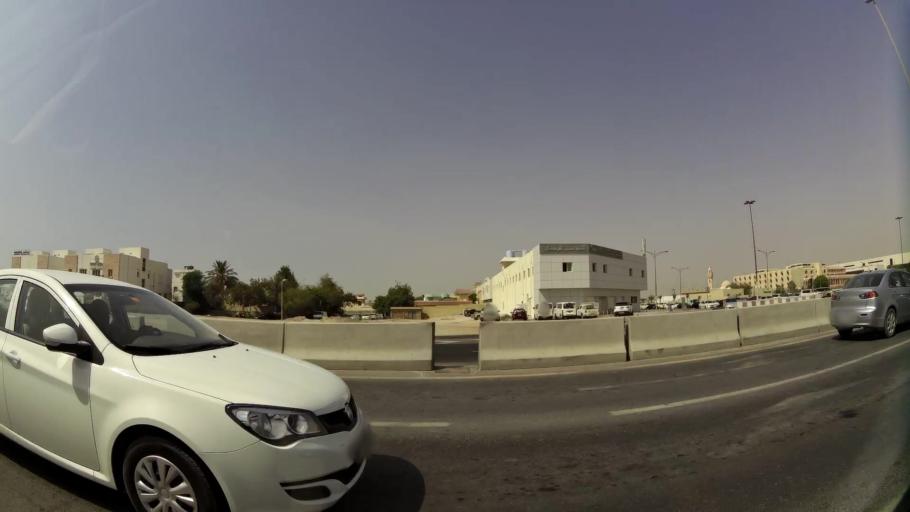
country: AE
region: Ash Shariqah
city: Sharjah
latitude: 25.3409
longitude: 55.4286
